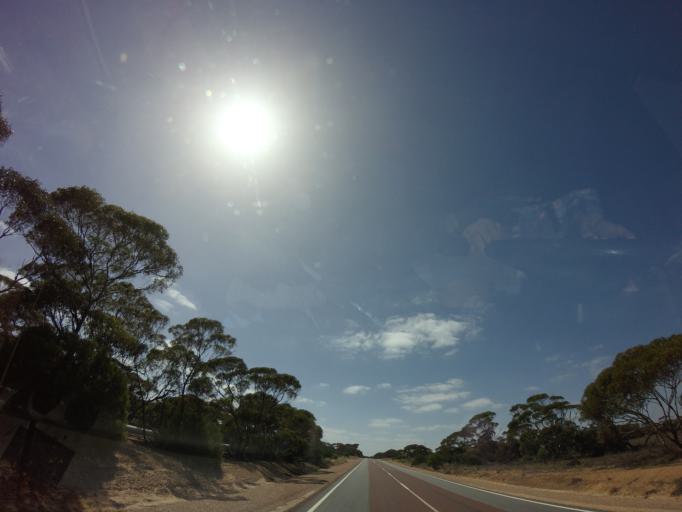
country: AU
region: South Australia
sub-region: Kimba
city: Caralue
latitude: -33.0882
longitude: 135.5077
